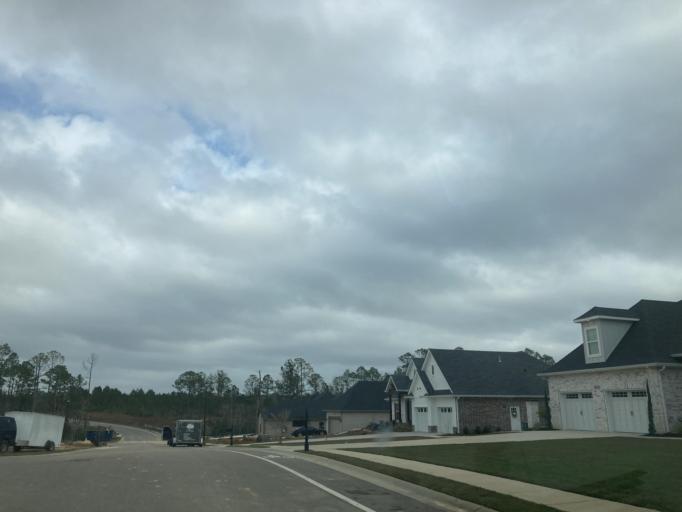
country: US
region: Mississippi
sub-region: Harrison County
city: D'Iberville
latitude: 30.4867
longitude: -88.9966
